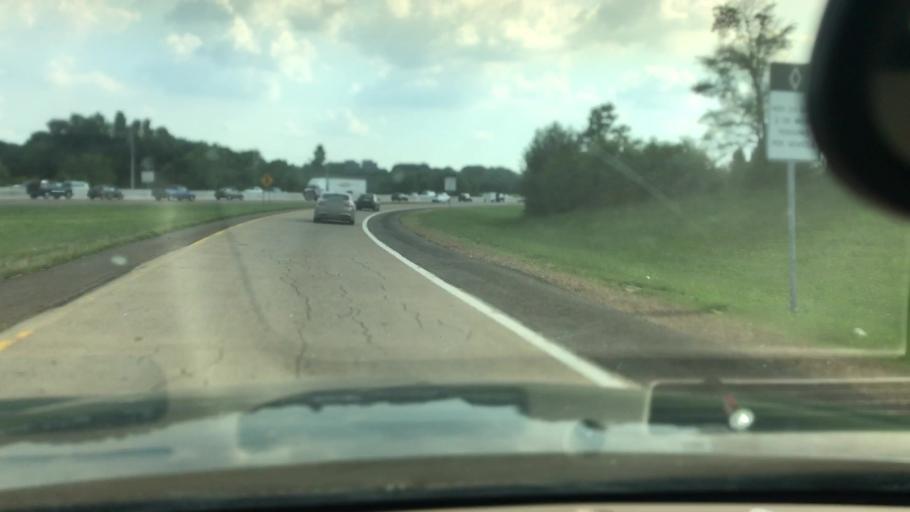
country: US
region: Tennessee
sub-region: Shelby County
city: Bartlett
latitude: 35.1854
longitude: -89.8156
